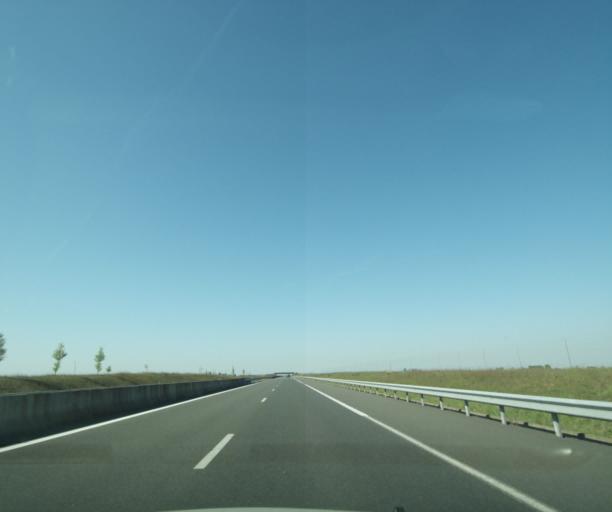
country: FR
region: Centre
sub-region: Departement du Loiret
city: Ascheres-le-Marche
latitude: 48.0840
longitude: 1.9929
